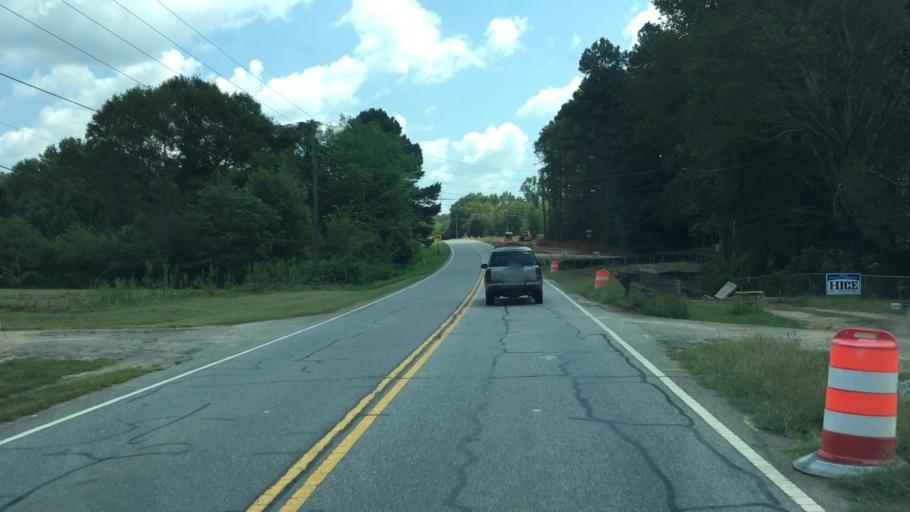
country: US
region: Georgia
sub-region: Barrow County
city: Statham
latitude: 33.9157
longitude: -83.6034
